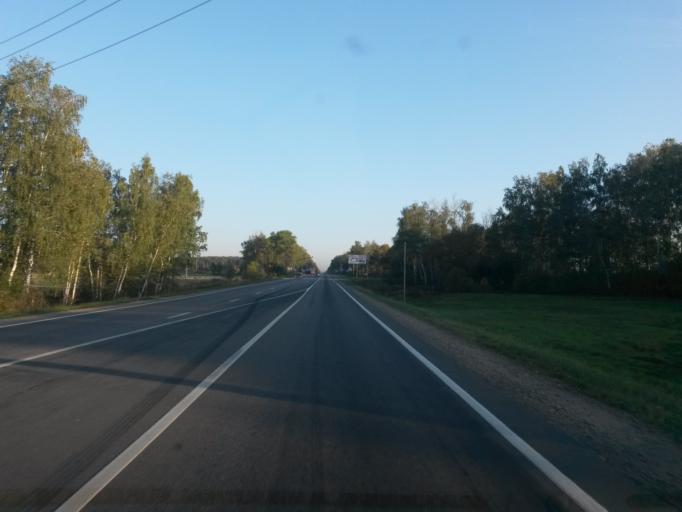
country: RU
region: Moskovskaya
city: Belyye Stolby
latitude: 55.2748
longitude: 37.8259
